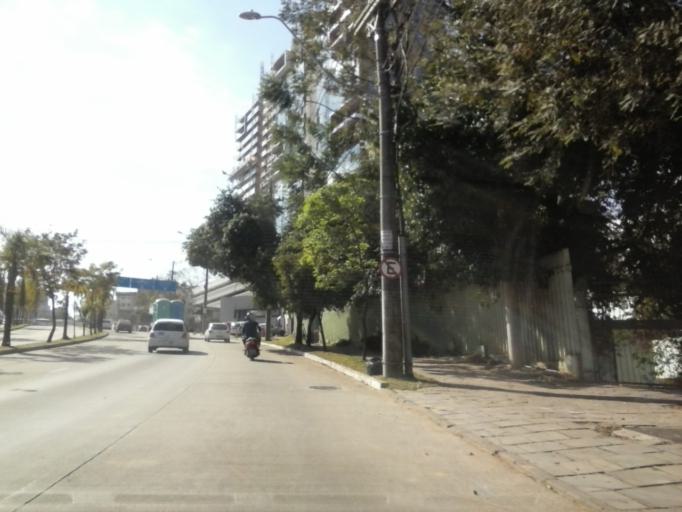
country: BR
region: Rio Grande do Sul
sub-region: Porto Alegre
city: Porto Alegre
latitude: -30.0420
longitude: -51.1732
